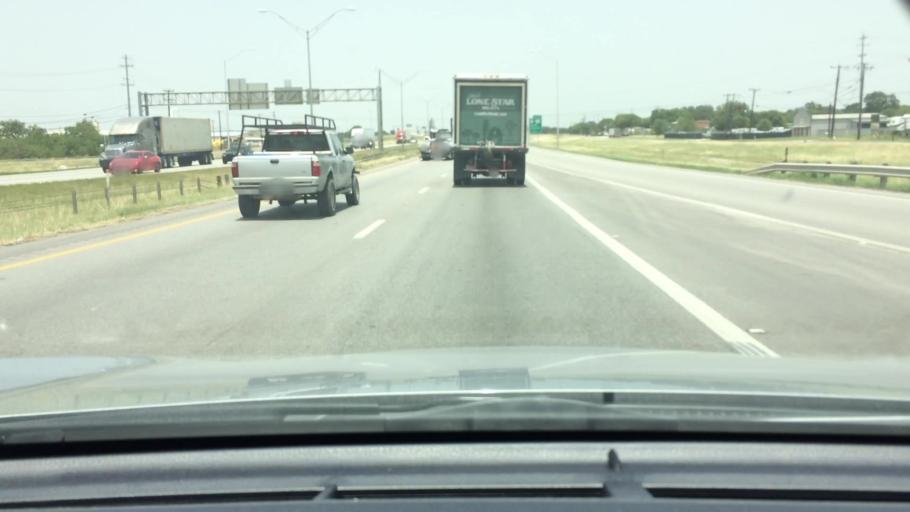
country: US
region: Texas
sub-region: Bexar County
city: Kirby
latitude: 29.4261
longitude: -98.3891
